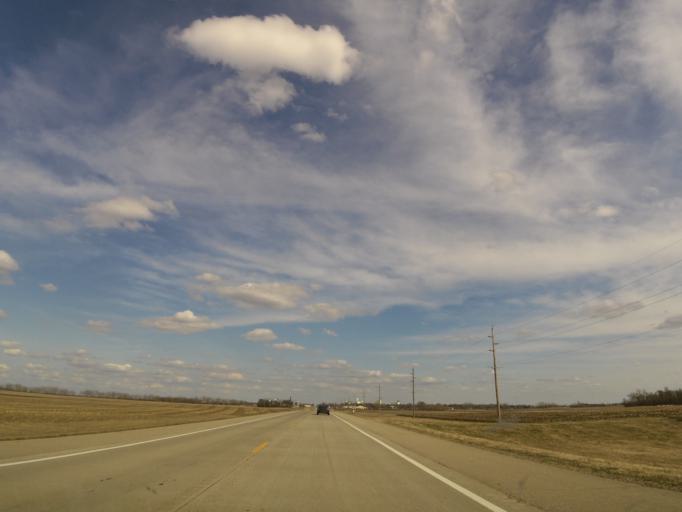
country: US
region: Minnesota
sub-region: Lac qui Parle County
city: Dawson
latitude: 44.9356
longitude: -96.0943
